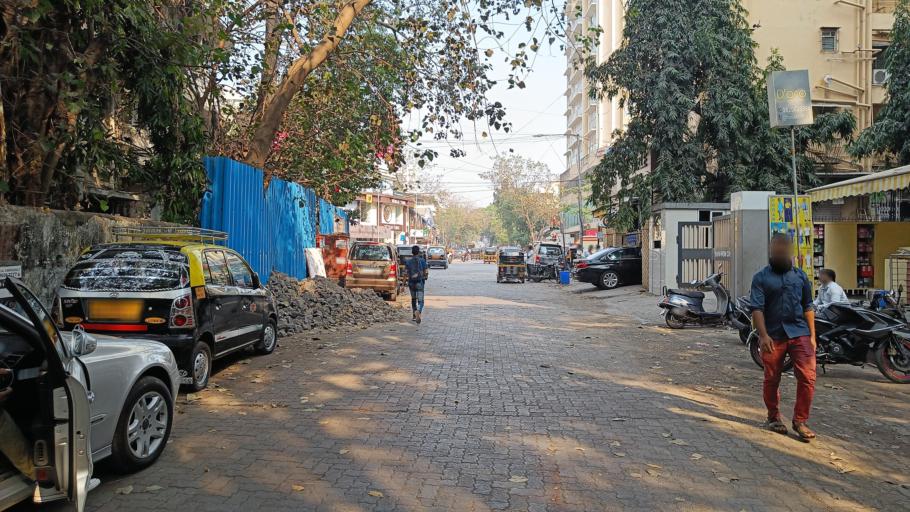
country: IN
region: Maharashtra
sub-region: Mumbai Suburban
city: Mumbai
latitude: 19.0827
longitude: 72.8374
